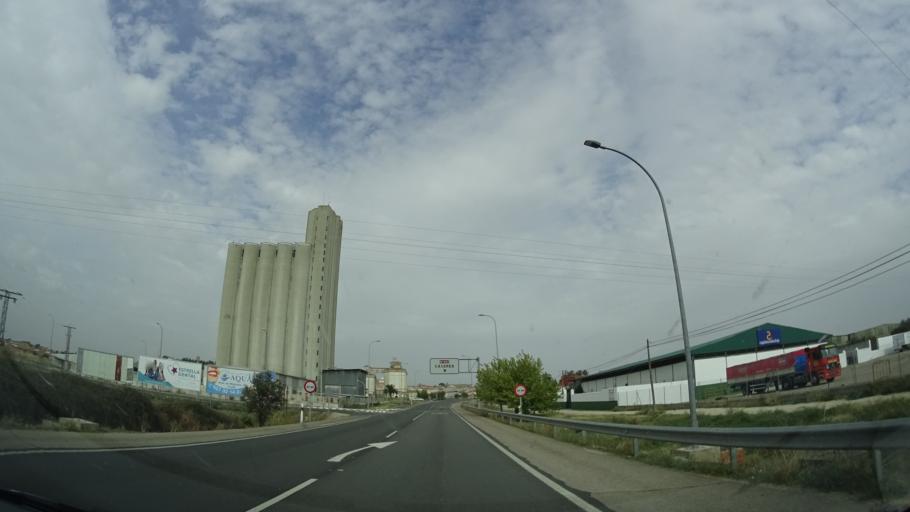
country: ES
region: Extremadura
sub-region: Provincia de Caceres
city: Trujillo
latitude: 39.4503
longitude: -5.8810
